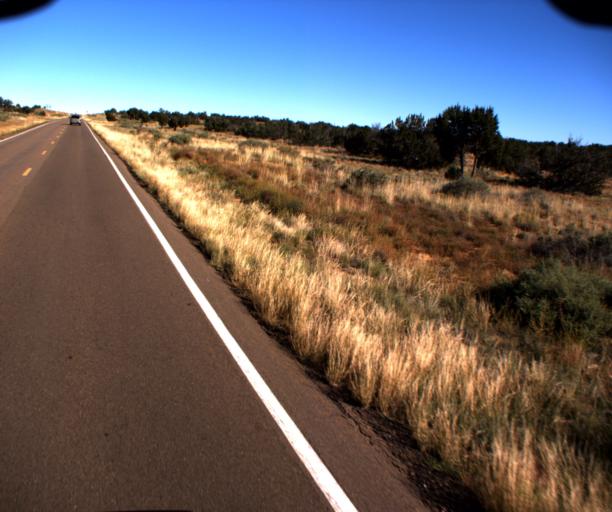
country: US
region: Arizona
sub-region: Navajo County
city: Snowflake
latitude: 34.6155
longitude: -110.0911
